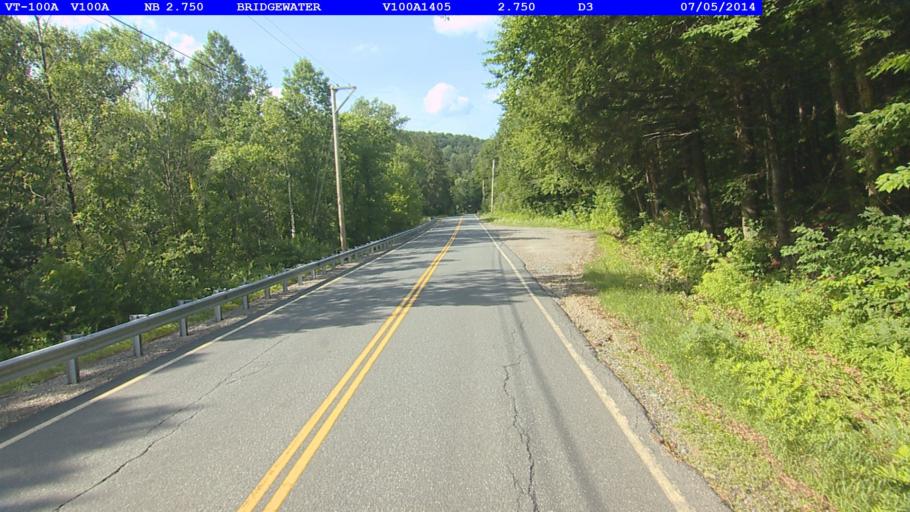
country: US
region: Vermont
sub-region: Windsor County
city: Woodstock
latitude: 43.5539
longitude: -72.7072
